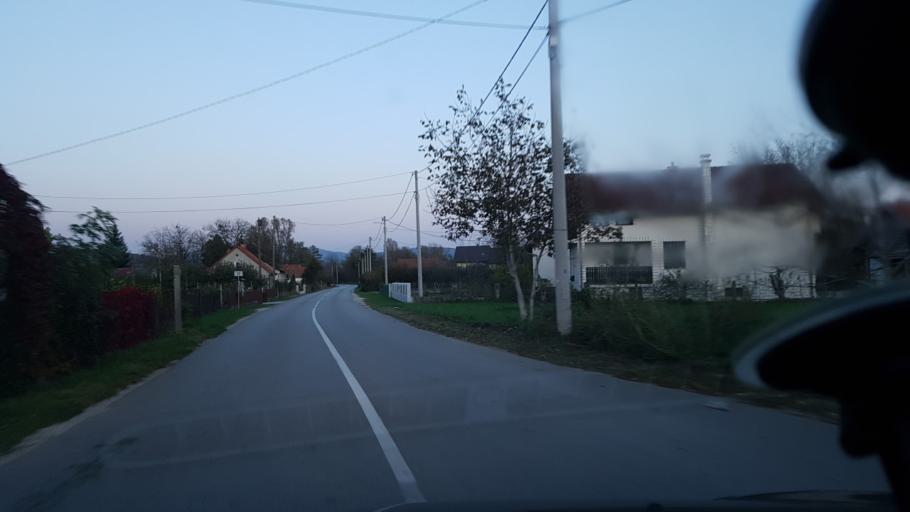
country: HR
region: Zagrebacka
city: Bregana
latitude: 45.8691
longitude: 15.7261
